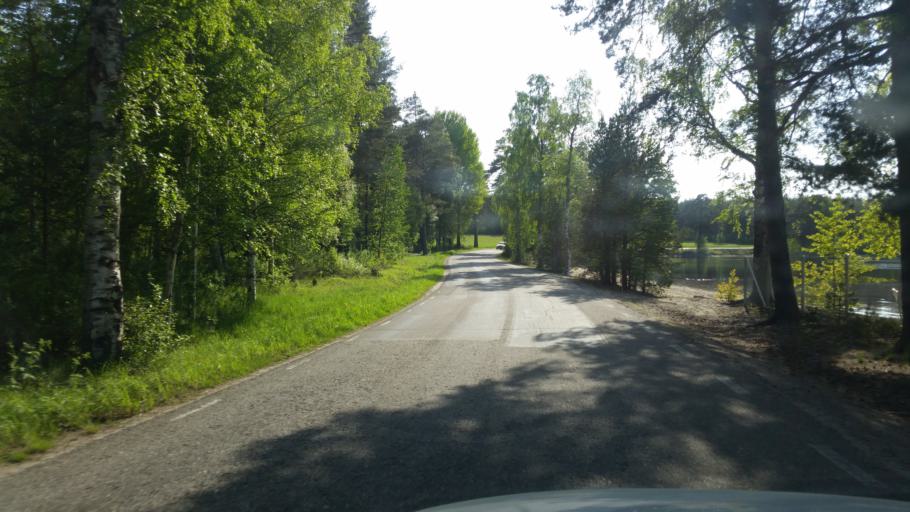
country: SE
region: Gaevleborg
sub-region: Hudiksvalls Kommun
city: Delsbo
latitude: 61.8564
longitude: 16.6069
